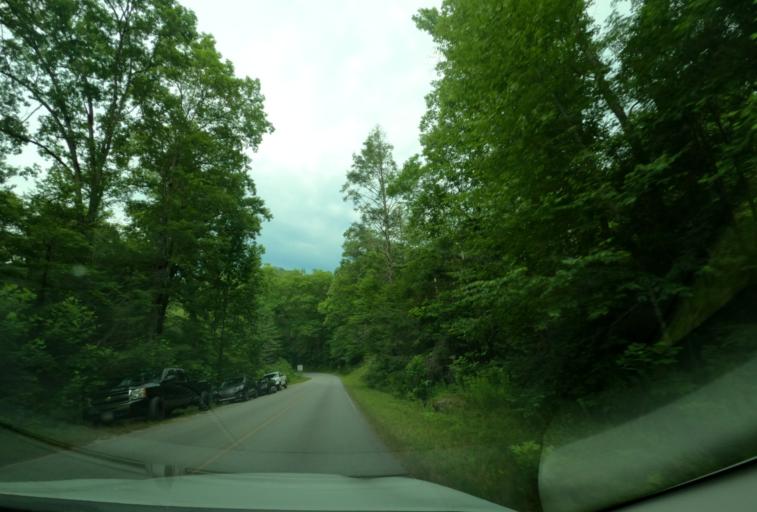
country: US
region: North Carolina
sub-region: Transylvania County
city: Brevard
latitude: 35.2825
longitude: -82.8159
